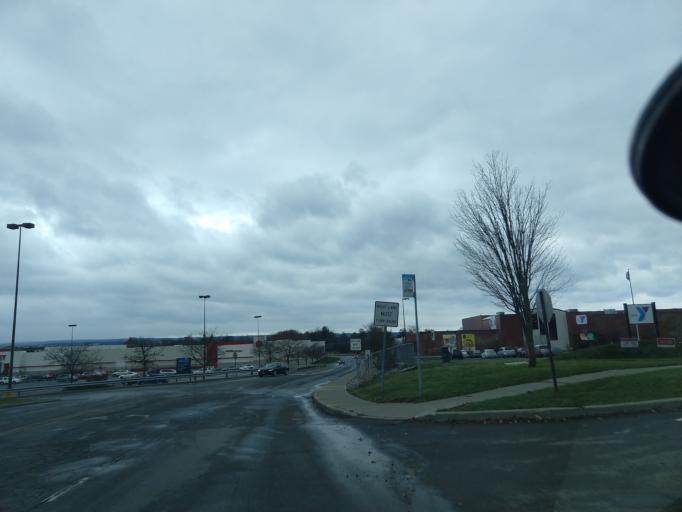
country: US
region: New York
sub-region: Tompkins County
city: Lansing
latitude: 42.4860
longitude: -76.4886
